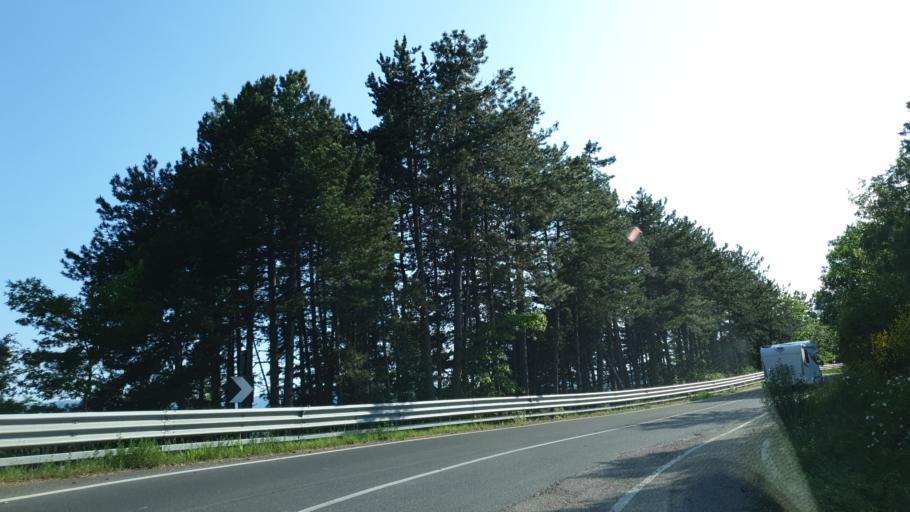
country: IT
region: Tuscany
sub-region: Province of Arezzo
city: Stia
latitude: 43.7751
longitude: 11.6915
